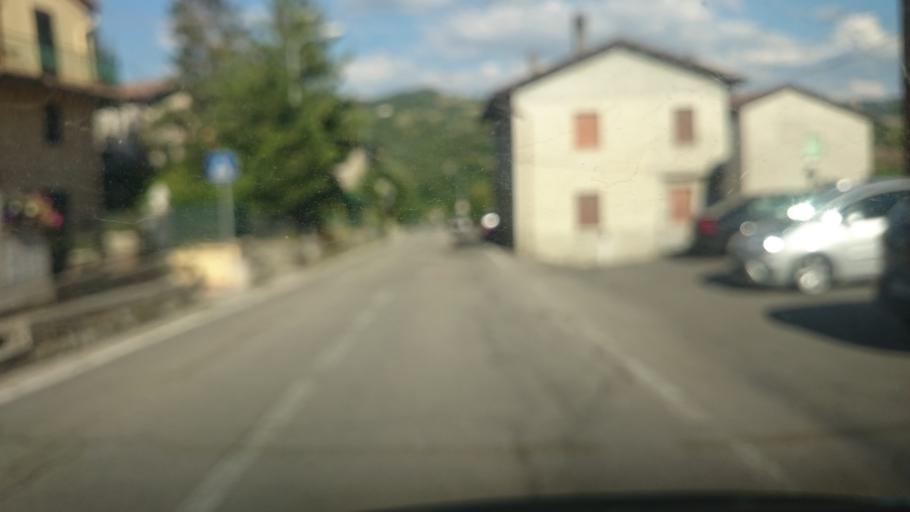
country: IT
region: Emilia-Romagna
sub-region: Provincia di Reggio Emilia
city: Villa Minozzo
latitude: 44.3887
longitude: 10.4654
